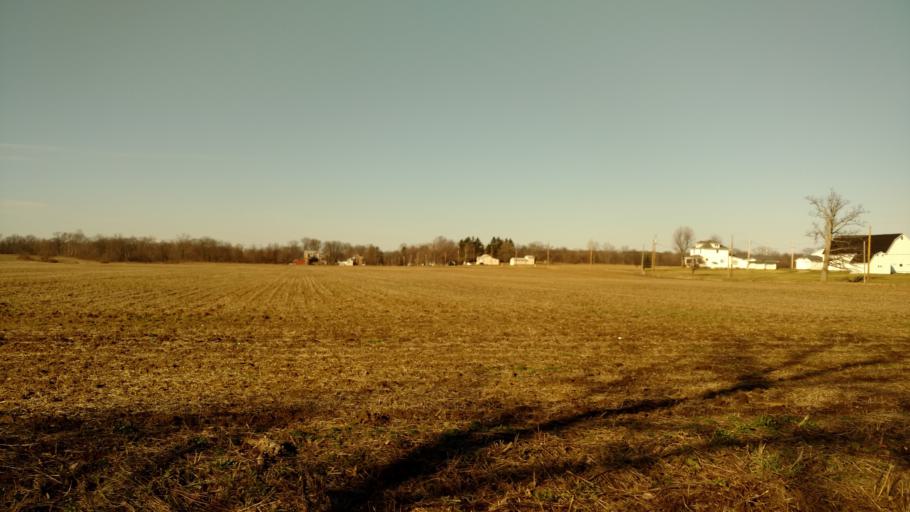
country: US
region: Ohio
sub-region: Crawford County
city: Galion
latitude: 40.6974
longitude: -82.7849
